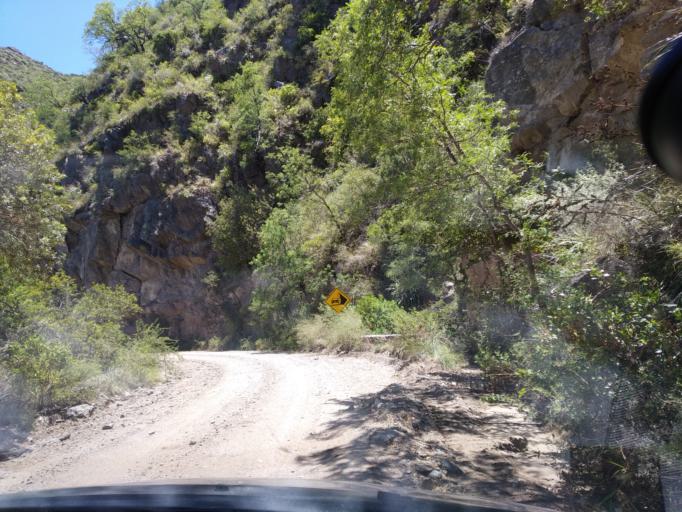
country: AR
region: Cordoba
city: Salsacate
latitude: -31.3717
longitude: -65.4059
